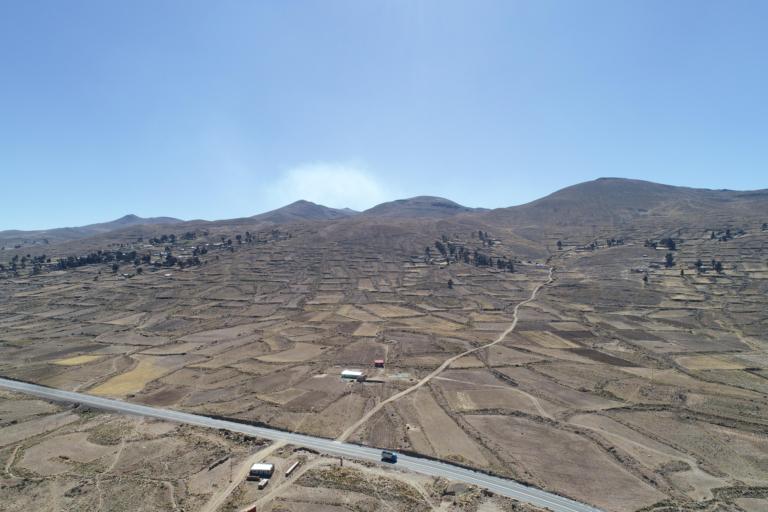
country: BO
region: La Paz
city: Achacachi
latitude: -15.8861
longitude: -68.8130
